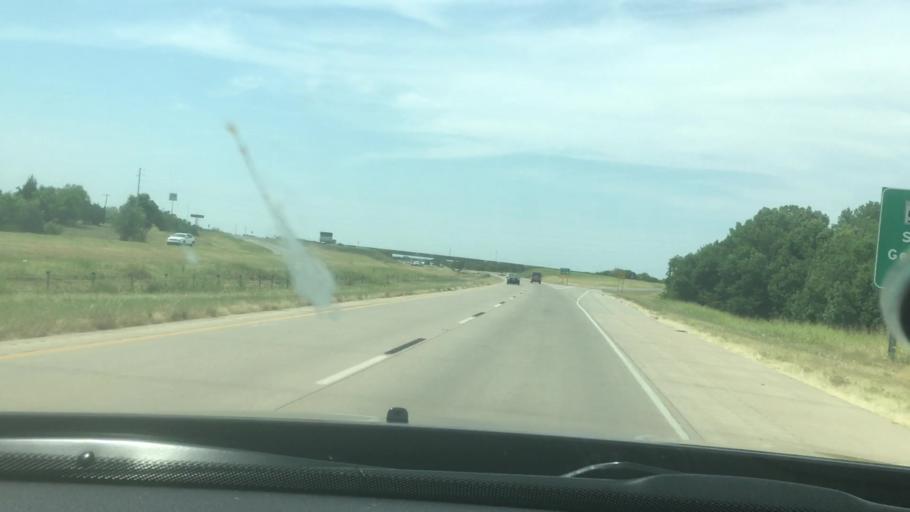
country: US
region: Oklahoma
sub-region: Carter County
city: Ardmore
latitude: 34.3080
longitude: -97.1596
